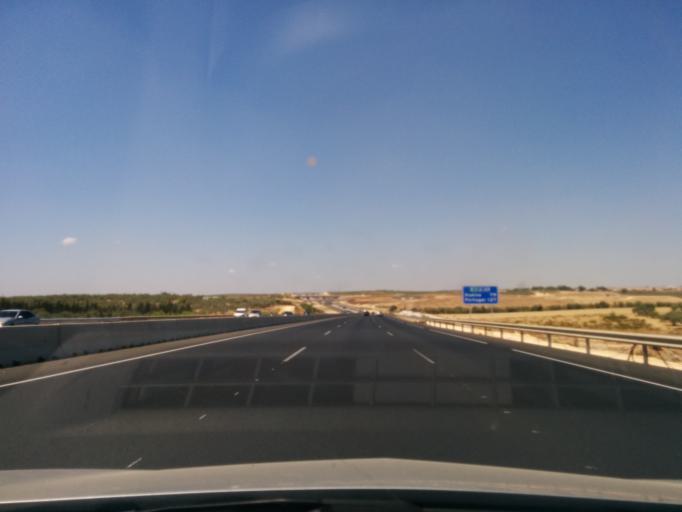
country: ES
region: Andalusia
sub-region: Provincia de Sevilla
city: Bormujos
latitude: 37.3734
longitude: -6.0883
